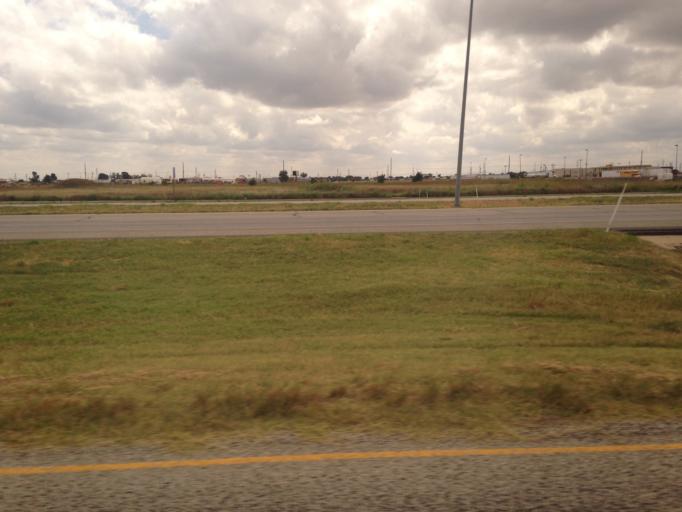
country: US
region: Texas
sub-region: Lubbock County
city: Lubbock
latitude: 33.5319
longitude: -101.8060
